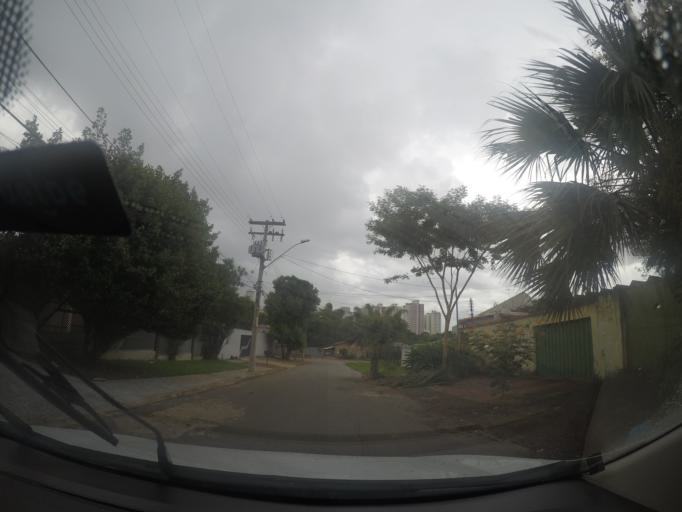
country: BR
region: Goias
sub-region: Goiania
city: Goiania
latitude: -16.6504
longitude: -49.2375
